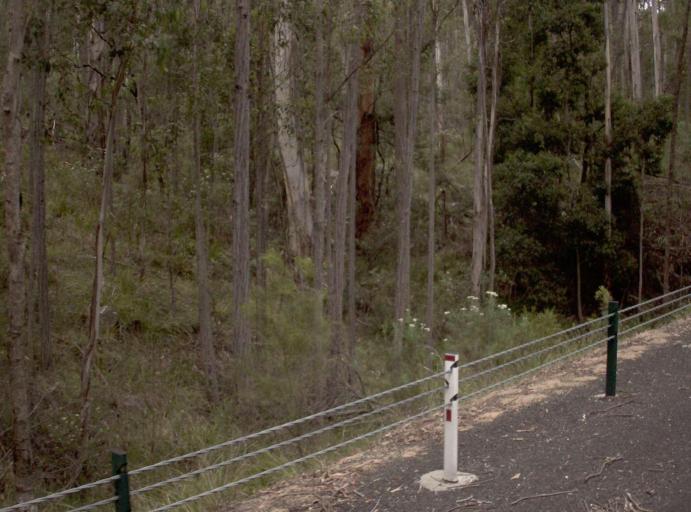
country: AU
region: New South Wales
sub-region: Bombala
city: Bombala
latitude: -37.3536
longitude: 149.2020
